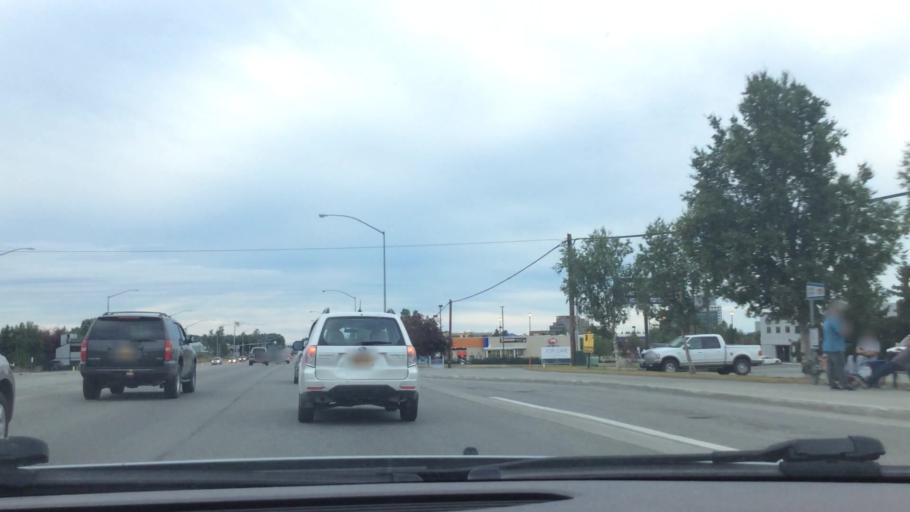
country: US
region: Alaska
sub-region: Anchorage Municipality
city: Anchorage
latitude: 61.1809
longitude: -149.8689
